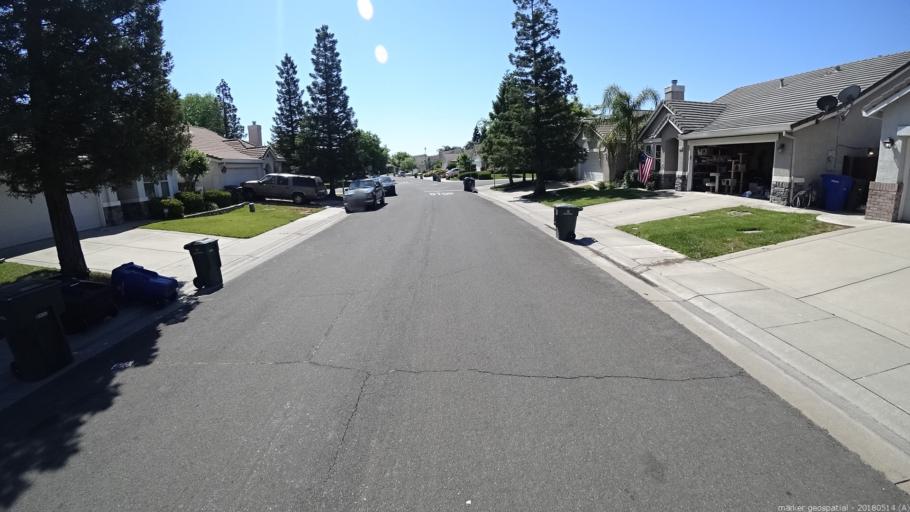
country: US
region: California
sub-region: Yolo County
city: West Sacramento
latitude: 38.6358
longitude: -121.5294
